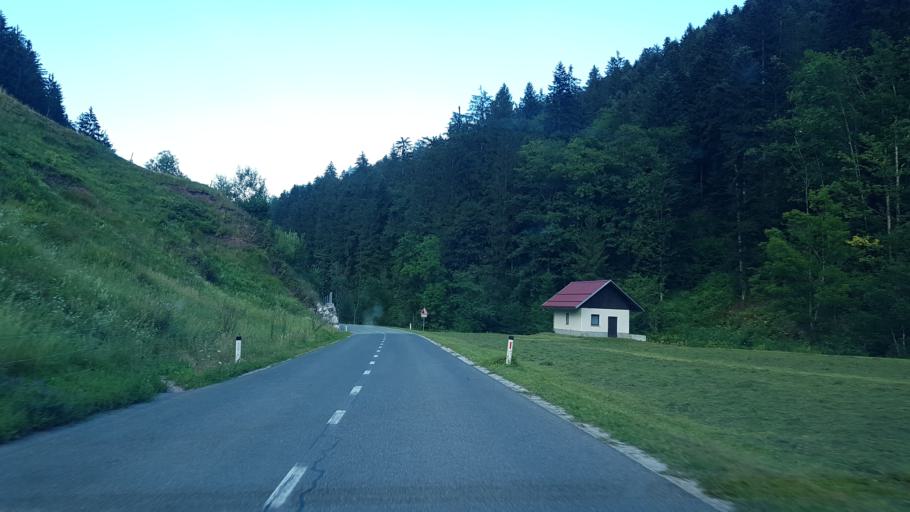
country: SI
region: Ziri
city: Ziri
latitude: 46.0808
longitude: 14.0761
